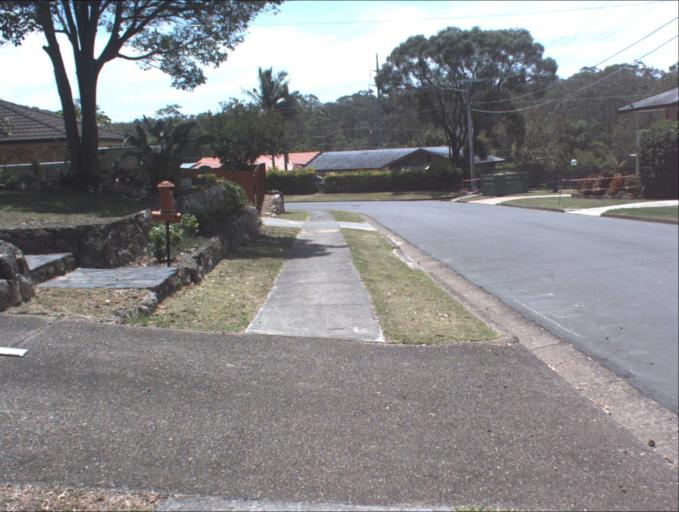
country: AU
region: Queensland
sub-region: Logan
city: Rochedale South
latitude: -27.5922
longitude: 153.1416
